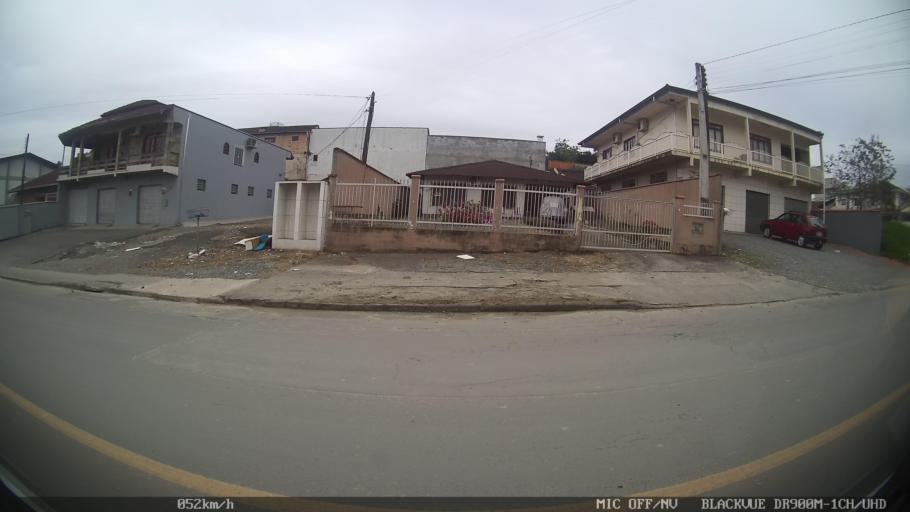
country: BR
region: Santa Catarina
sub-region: Joinville
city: Joinville
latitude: -26.2741
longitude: -48.8884
